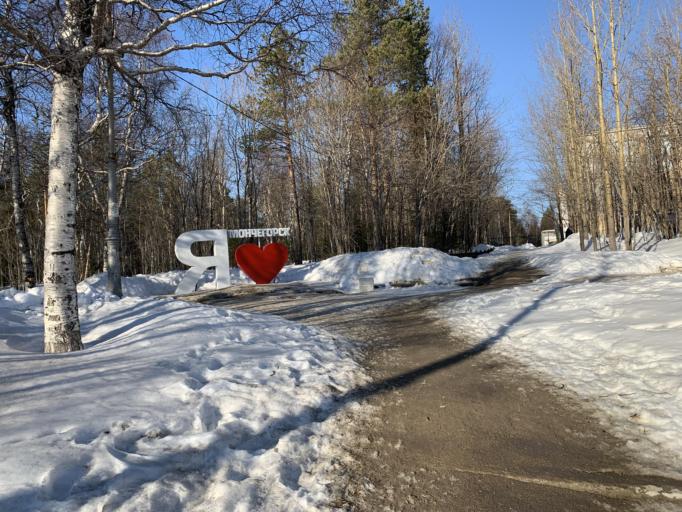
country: RU
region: Murmansk
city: Monchegorsk
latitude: 67.9391
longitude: 32.9349
